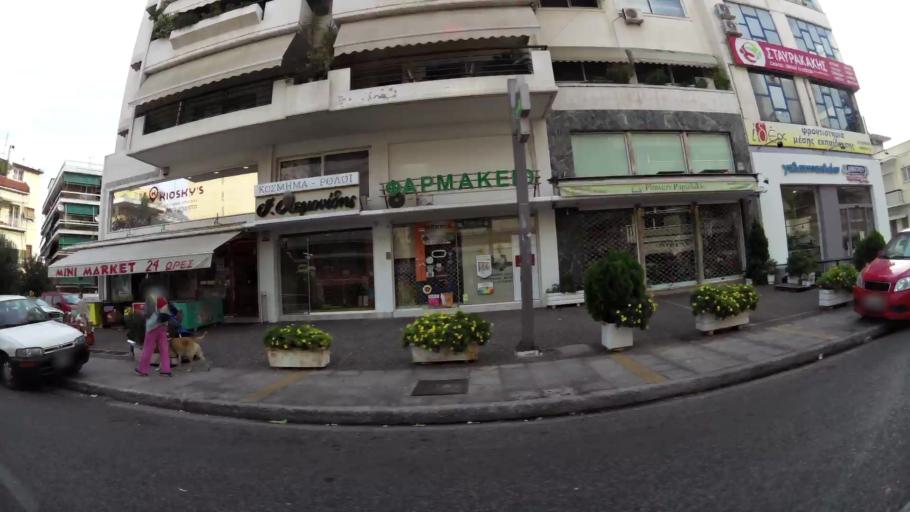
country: GR
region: Attica
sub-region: Nomarchia Athinas
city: Palaio Faliro
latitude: 37.9332
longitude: 23.6993
